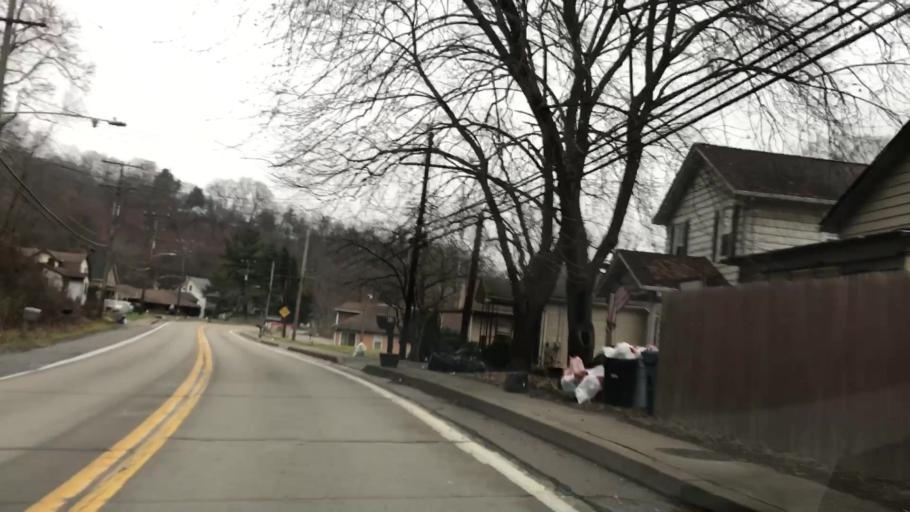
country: US
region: Pennsylvania
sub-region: Allegheny County
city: Leetsdale
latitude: 40.5532
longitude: -80.2192
